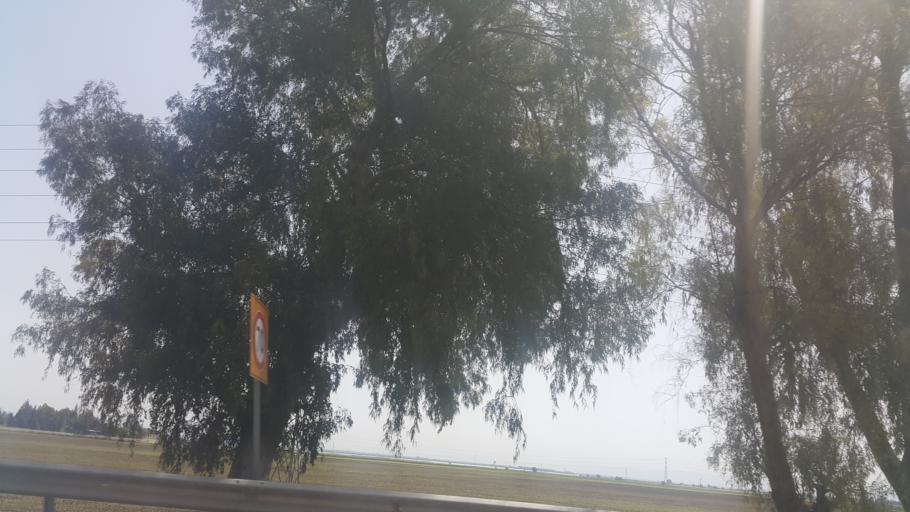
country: TR
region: Hatay
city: Serinyol
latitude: 36.3822
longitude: 36.2296
